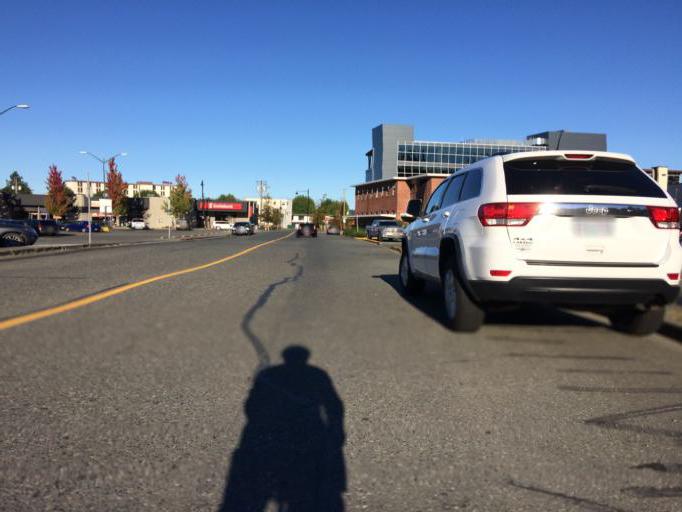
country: CA
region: British Columbia
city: Campbell River
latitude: 50.0244
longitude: -125.2451
